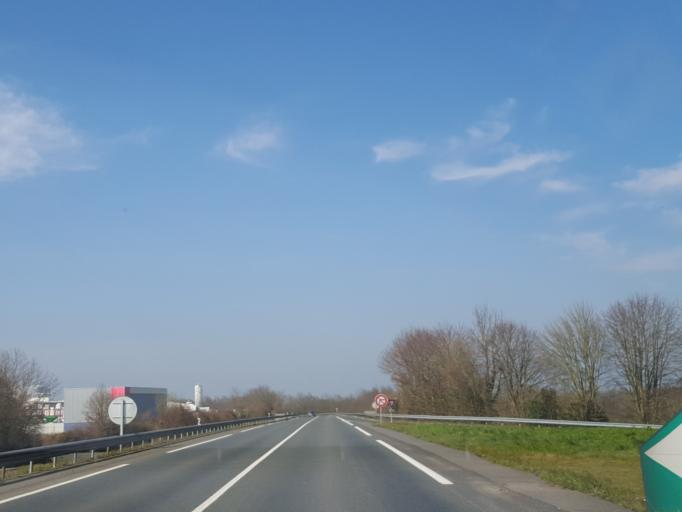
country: FR
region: Pays de la Loire
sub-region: Departement de la Vendee
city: Saint-Fulgent
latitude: 46.8584
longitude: -1.1709
